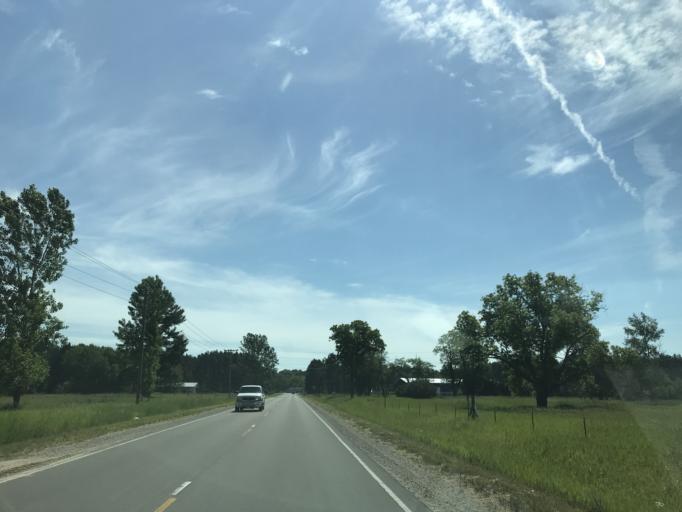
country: US
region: Michigan
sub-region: Grand Traverse County
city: Traverse City
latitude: 44.6542
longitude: -85.7018
